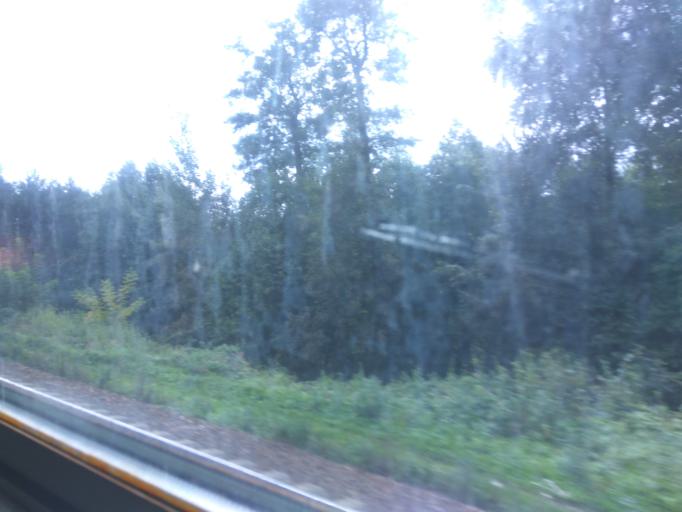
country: RU
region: Moskovskaya
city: Beloozerskiy
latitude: 55.4539
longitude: 38.4702
